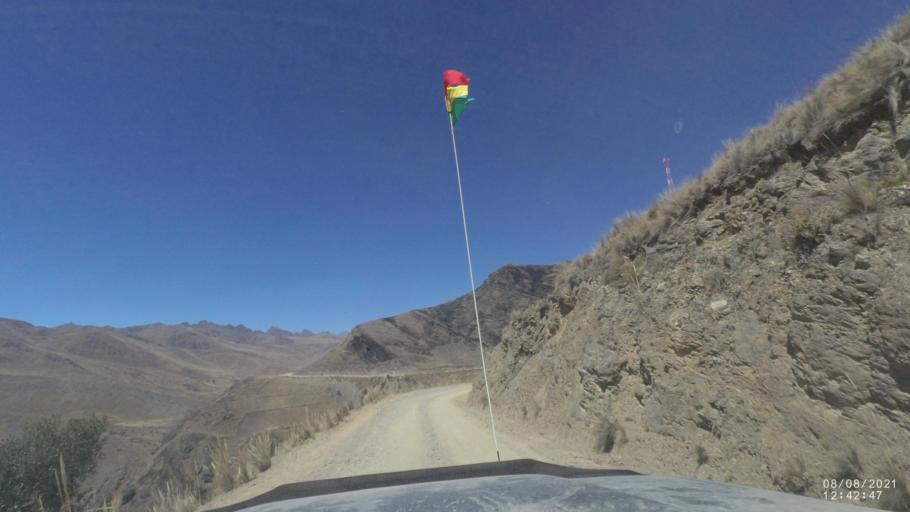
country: BO
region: Cochabamba
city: Colchani
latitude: -16.8407
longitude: -66.6145
